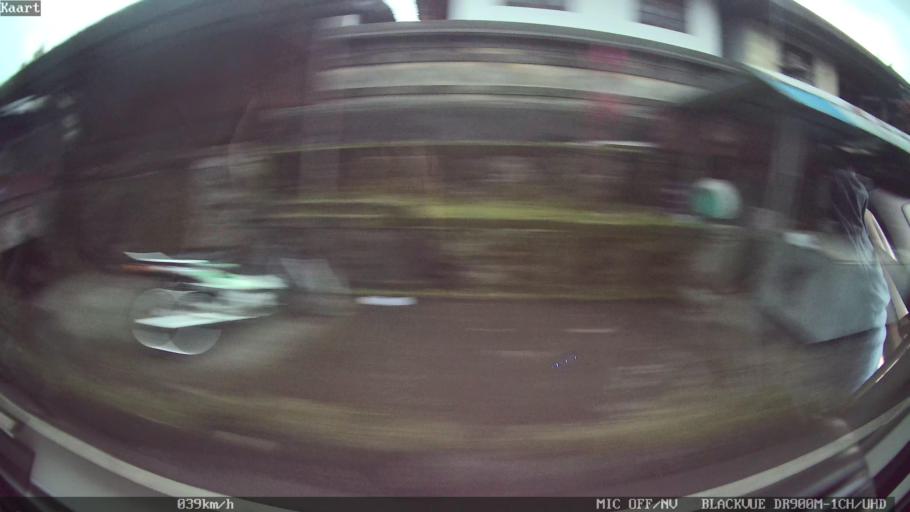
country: ID
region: Bali
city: Empalan
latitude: -8.3991
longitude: 115.1483
